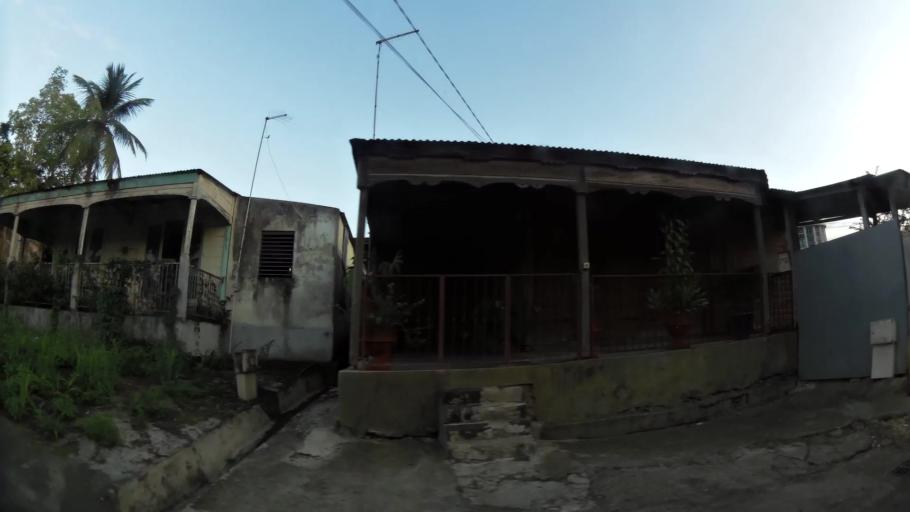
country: GP
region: Guadeloupe
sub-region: Guadeloupe
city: Les Abymes
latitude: 16.2690
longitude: -61.4960
